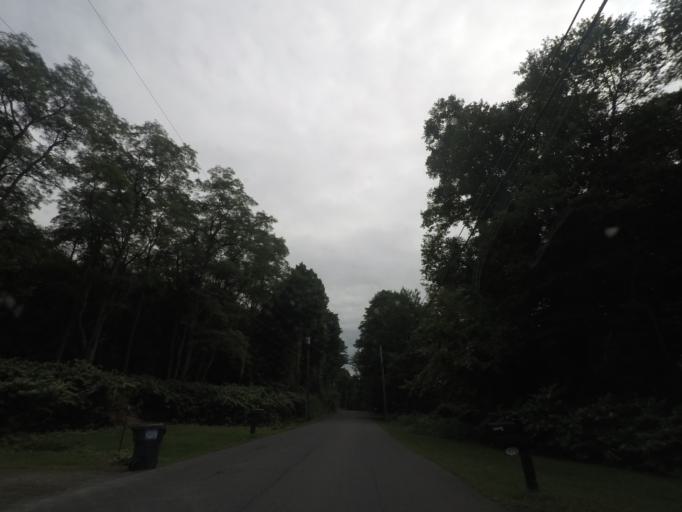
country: US
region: New York
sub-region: Rensselaer County
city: Nassau
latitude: 42.5067
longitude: -73.6078
